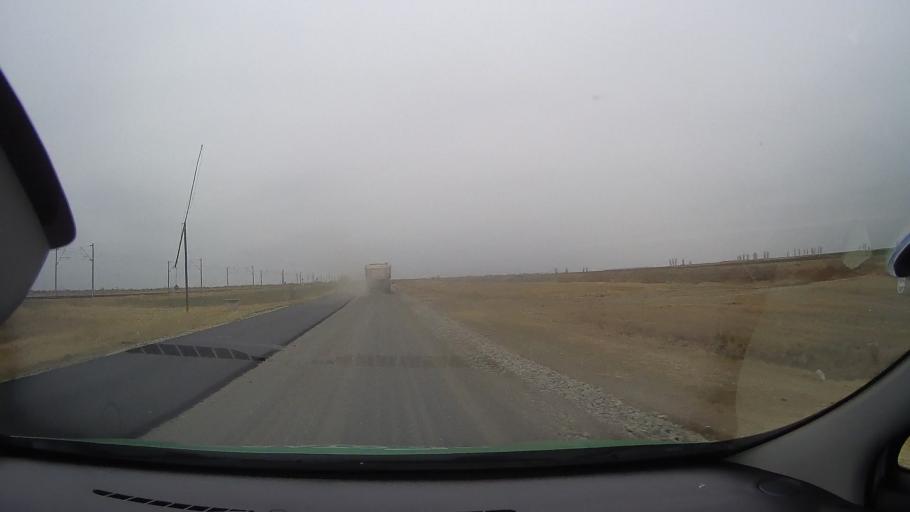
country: RO
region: Braila
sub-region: Comuna Baraganul
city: Baraganul
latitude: 44.7972
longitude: 27.5303
